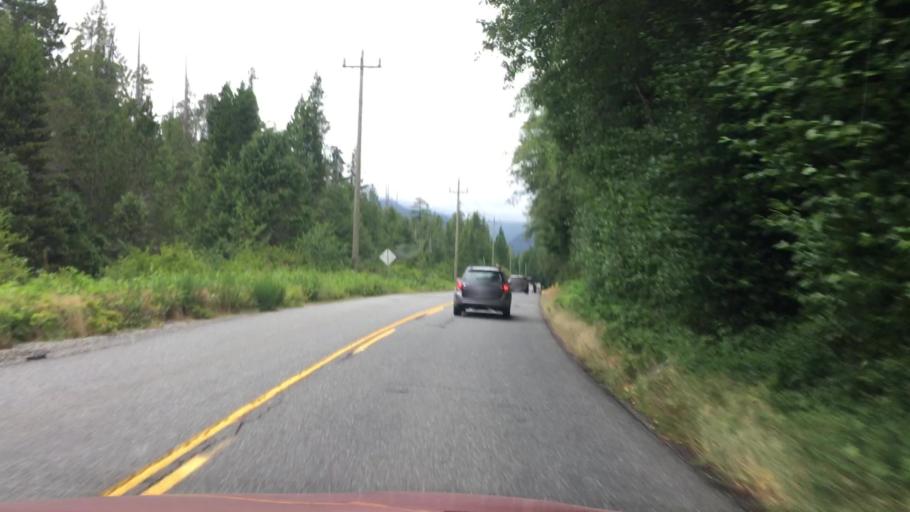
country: CA
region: British Columbia
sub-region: Regional District of Alberni-Clayoquot
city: Ucluelet
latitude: 49.0860
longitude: -125.4580
